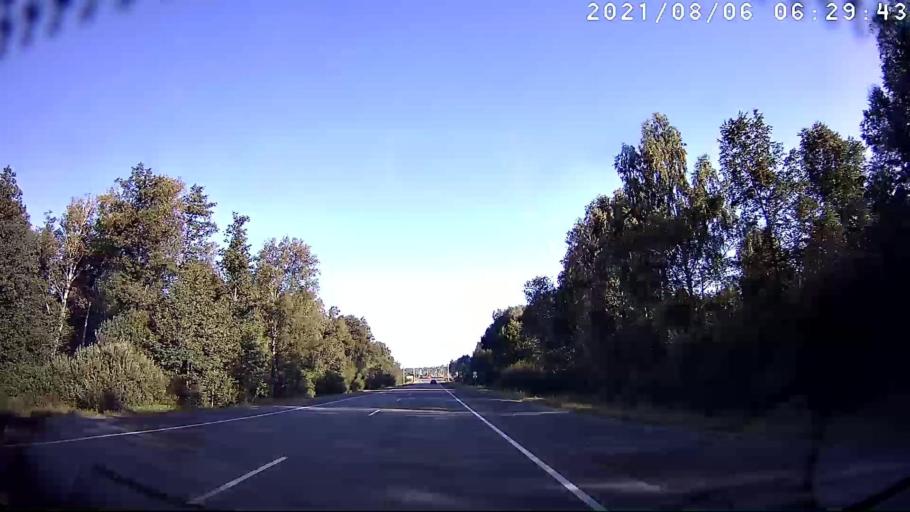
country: RU
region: Mariy-El
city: Krasnogorskiy
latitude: 56.1592
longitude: 48.2925
